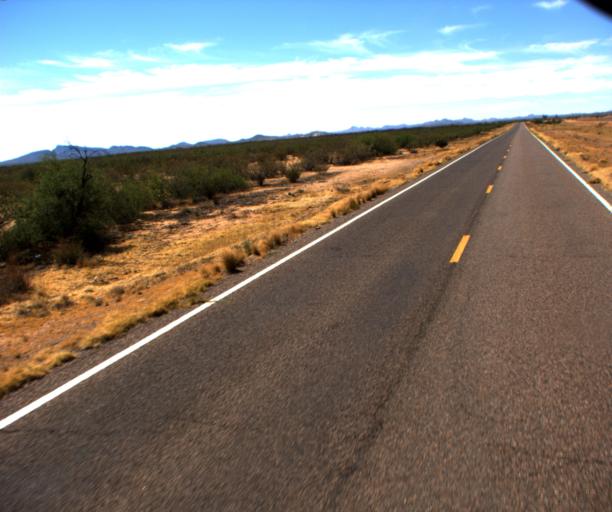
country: US
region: Arizona
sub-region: Yavapai County
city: Congress
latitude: 33.9597
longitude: -113.1416
